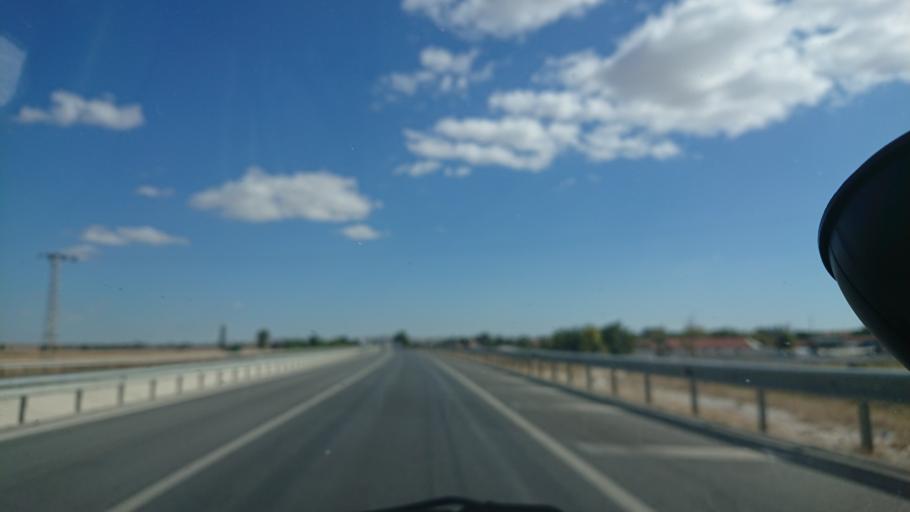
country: TR
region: Eskisehir
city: Mahmudiye
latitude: 39.5436
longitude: 30.9350
